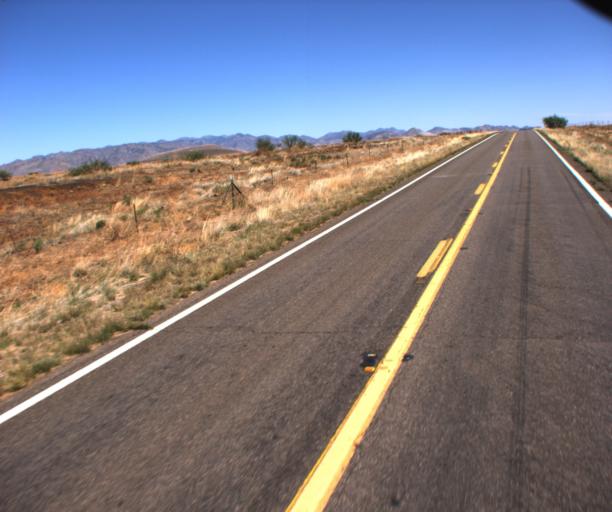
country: US
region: Arizona
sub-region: Cochise County
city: Douglas
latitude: 31.5671
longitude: -109.2629
